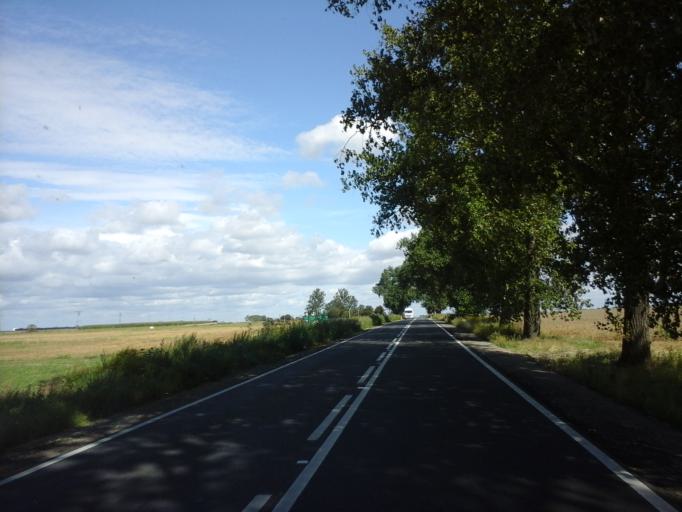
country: PL
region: West Pomeranian Voivodeship
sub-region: Powiat stargardzki
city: Stargard Szczecinski
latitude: 53.2565
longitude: 15.0999
